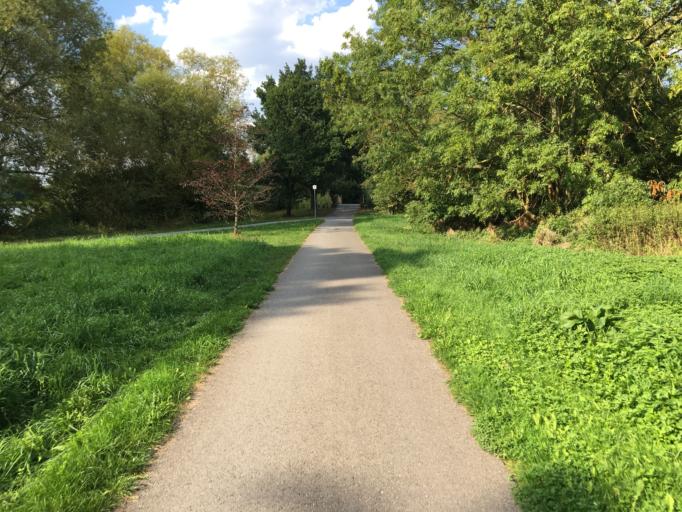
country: DE
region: Lower Saxony
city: Leiferde
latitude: 52.2261
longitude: 10.5142
